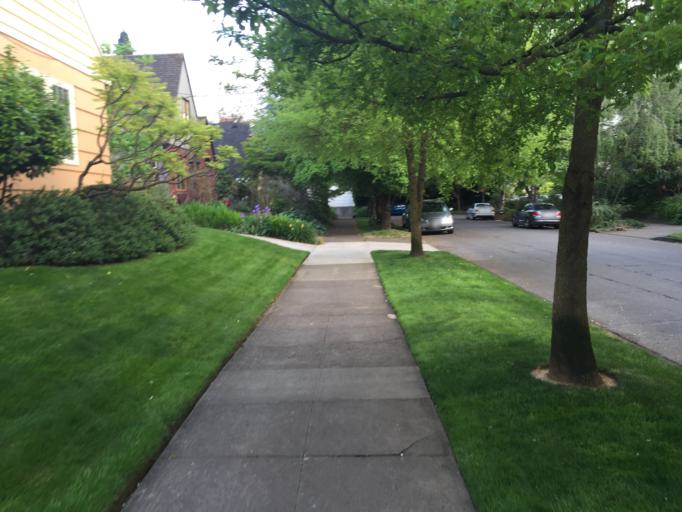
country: US
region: Oregon
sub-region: Multnomah County
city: Portland
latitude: 45.5104
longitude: -122.6381
